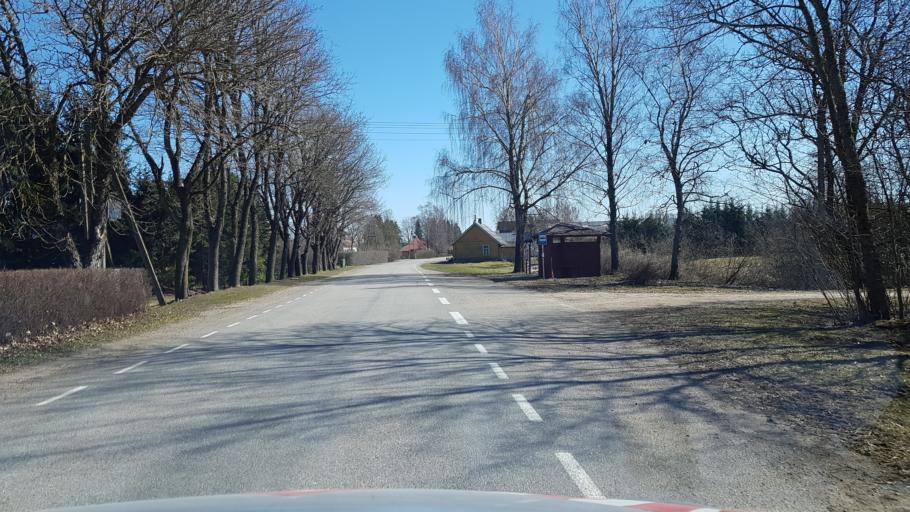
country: EE
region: Laeaene-Virumaa
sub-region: Vaeike-Maarja vald
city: Vaike-Maarja
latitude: 59.1136
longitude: 26.3691
